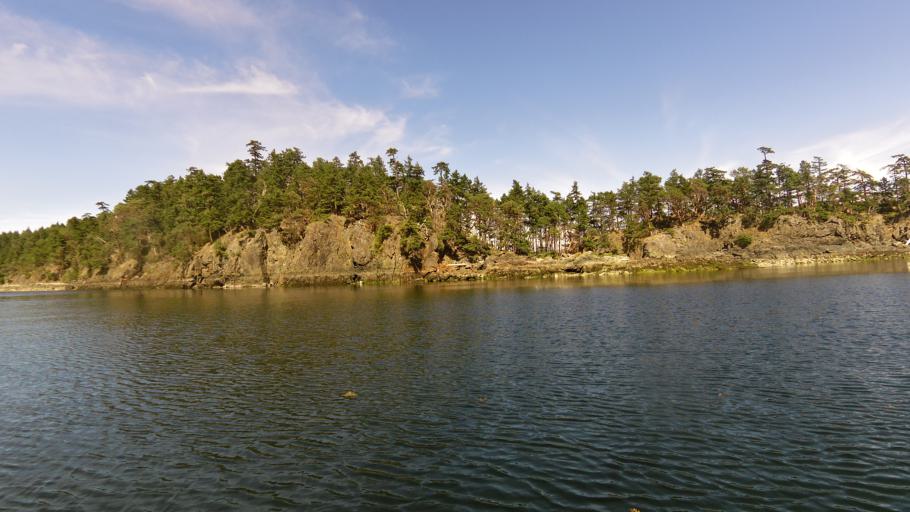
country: CA
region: British Columbia
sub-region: Regional District of Nanaimo
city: Parksville
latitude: 49.5164
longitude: -124.1364
